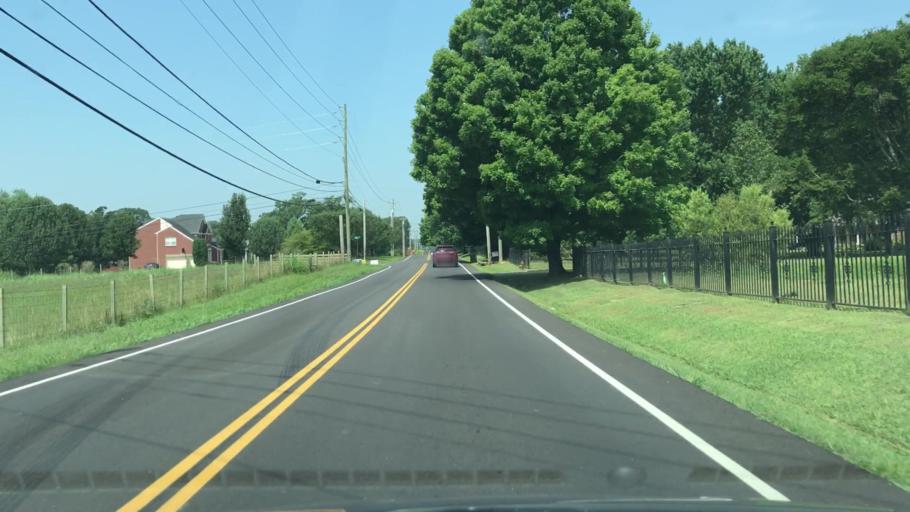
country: US
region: Tennessee
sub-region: Wilson County
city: Rural Hill
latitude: 36.1168
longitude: -86.4780
